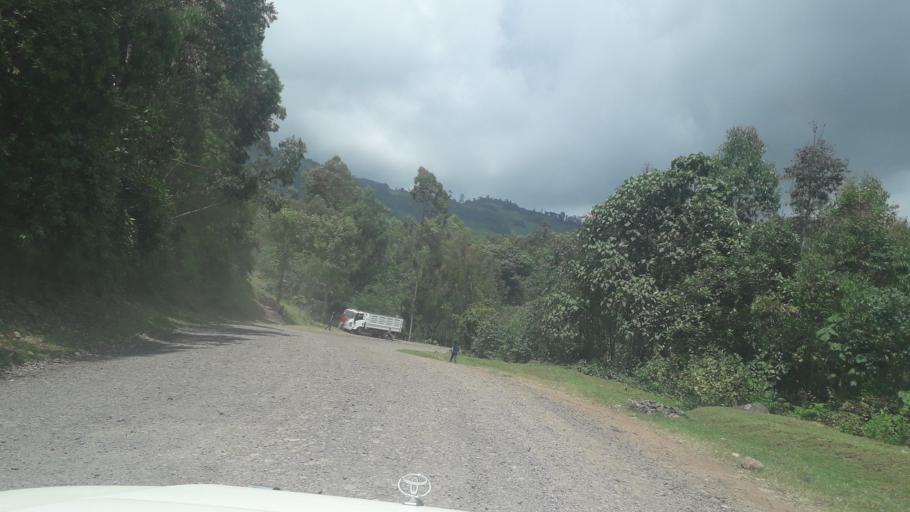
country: ET
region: Oromiya
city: Jima
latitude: 7.4265
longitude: 36.8723
